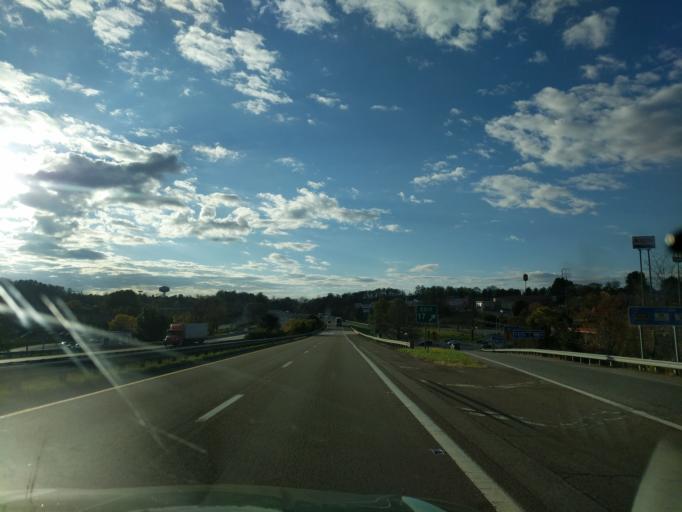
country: US
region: Virginia
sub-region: Washington County
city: Abingdon
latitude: 36.6995
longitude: -81.9712
